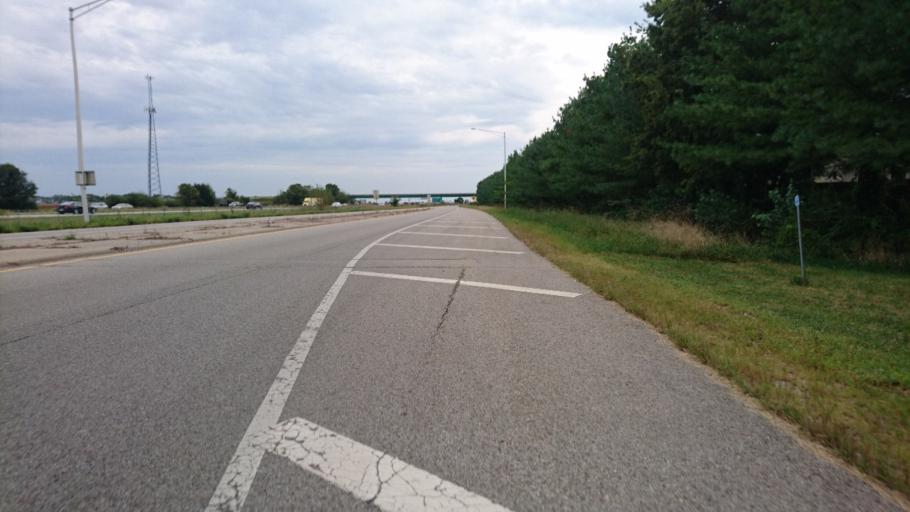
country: US
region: Illinois
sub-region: Sangamon County
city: Chatham
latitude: 39.6733
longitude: -89.6485
